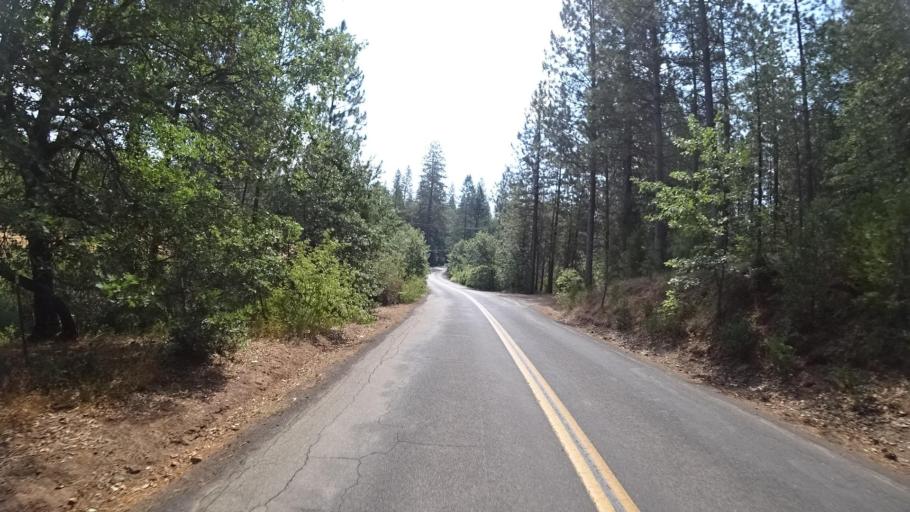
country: US
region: California
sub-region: Tuolumne County
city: Tuolumne City
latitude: 37.7716
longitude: -120.1617
